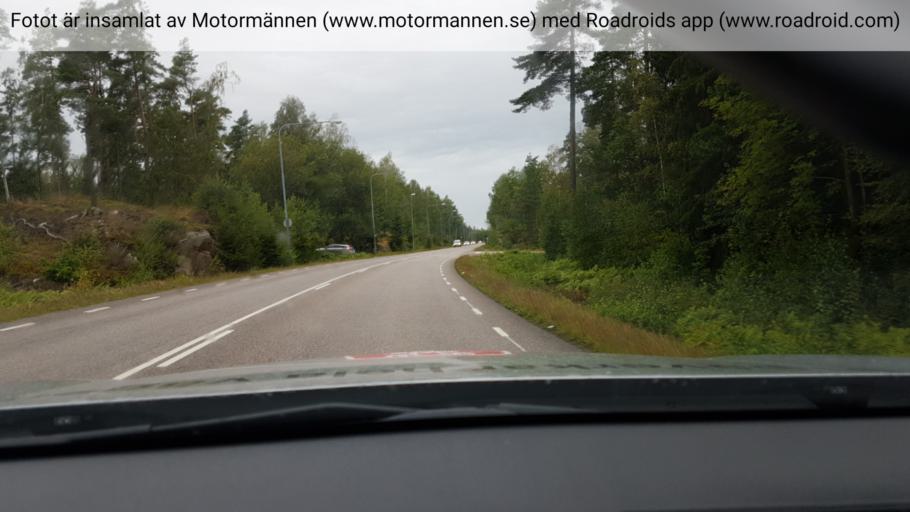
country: SE
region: Vaestra Goetaland
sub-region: Trollhattan
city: Trollhattan
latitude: 58.3124
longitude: 12.2786
